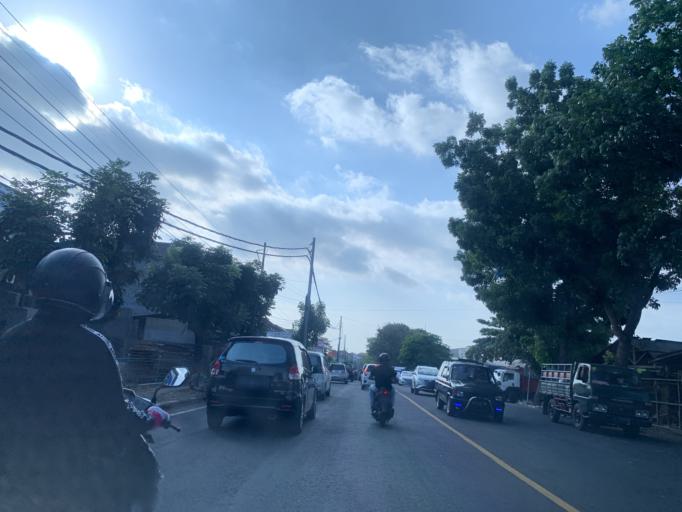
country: ID
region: Bali
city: Banjar Tegal Belodan
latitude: -8.5480
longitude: 115.1197
